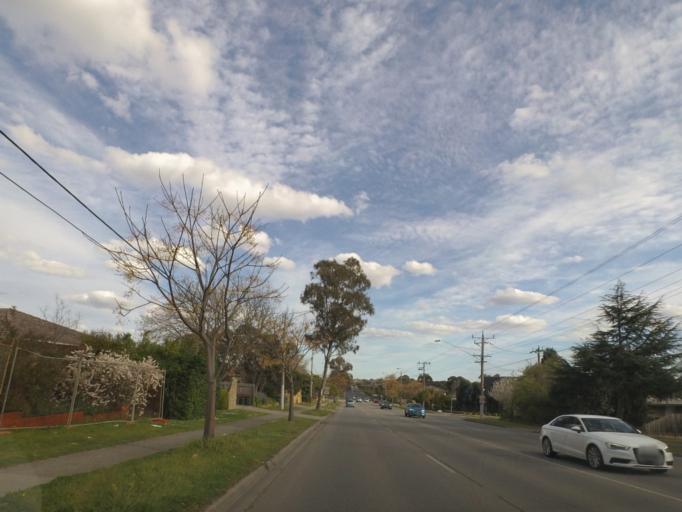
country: AU
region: Victoria
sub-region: Manningham
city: Doncaster East
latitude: -37.7884
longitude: 145.1436
